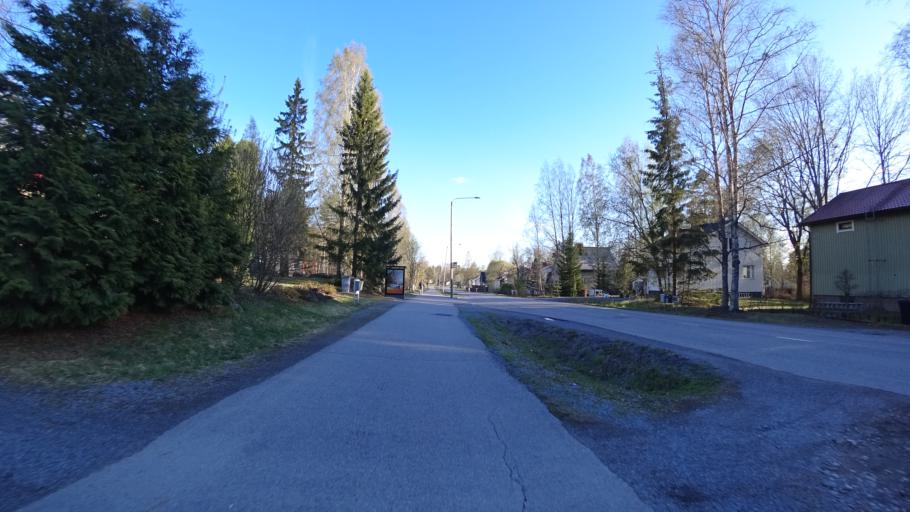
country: FI
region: Pirkanmaa
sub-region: Tampere
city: Yloejaervi
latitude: 61.5090
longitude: 23.5940
